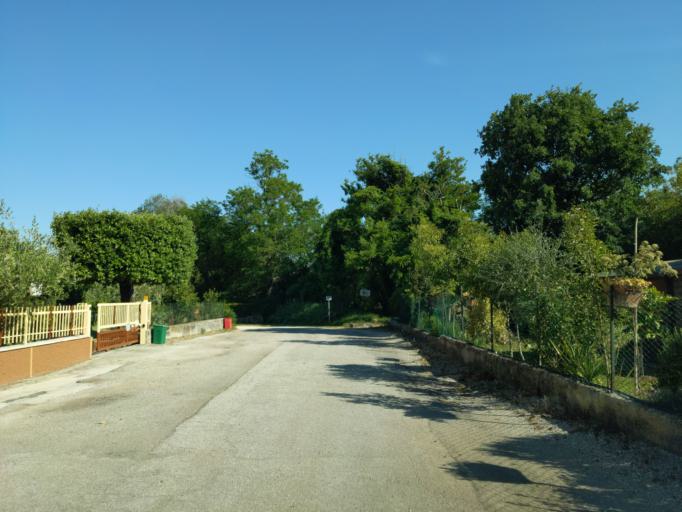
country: IT
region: The Marches
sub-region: Provincia di Pesaro e Urbino
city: Cuccurano
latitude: 43.7965
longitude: 12.9637
